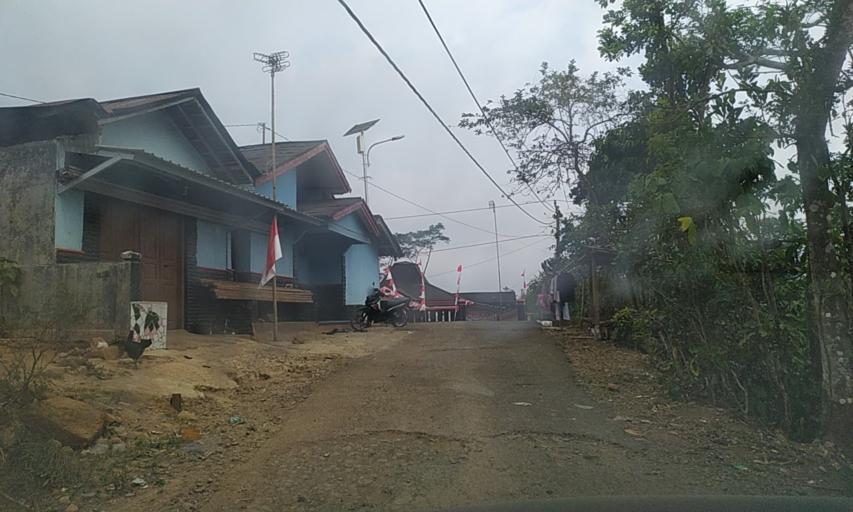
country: ID
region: Central Java
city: Randudongkal
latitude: -7.1891
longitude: 109.4221
